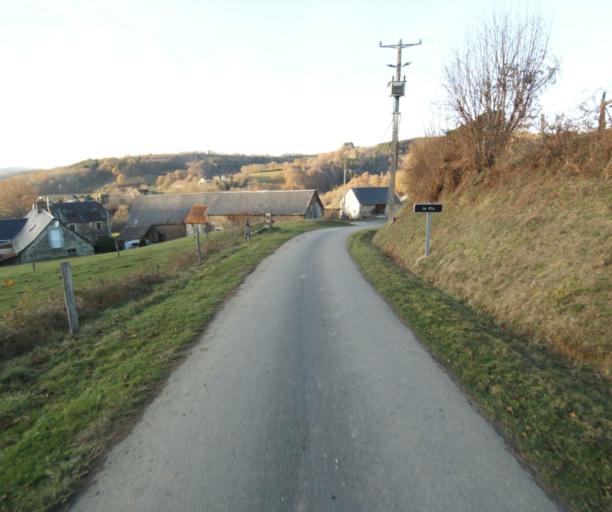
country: FR
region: Limousin
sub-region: Departement de la Correze
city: Laguenne
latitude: 45.2434
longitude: 1.8182
